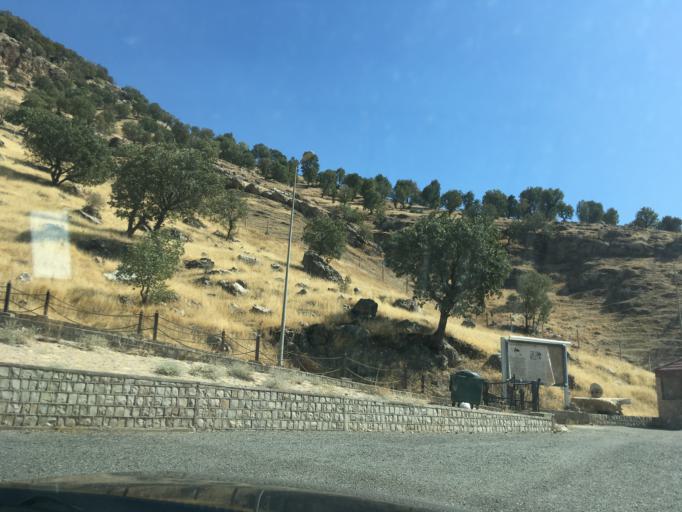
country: IQ
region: Arbil
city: Mergasur
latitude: 36.8327
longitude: 44.2179
